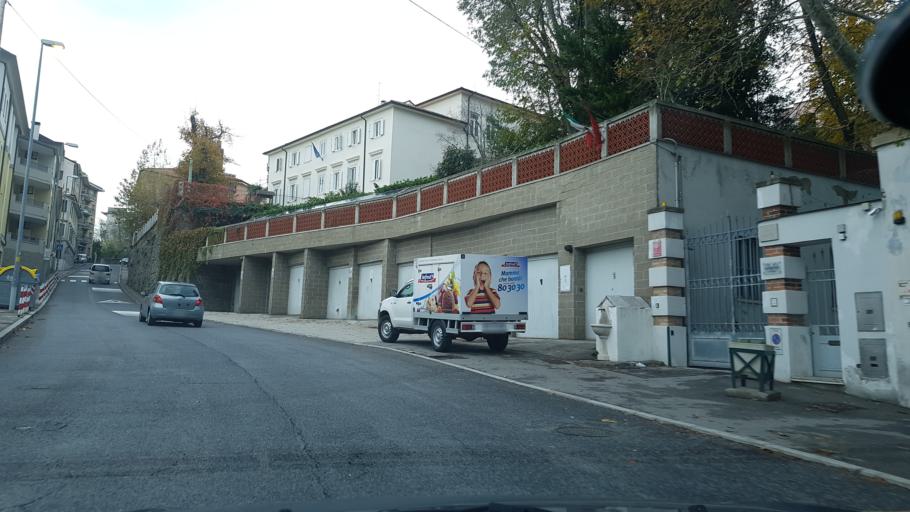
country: IT
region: Friuli Venezia Giulia
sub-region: Provincia di Trieste
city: Villa Opicina
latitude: 45.6650
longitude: 13.7691
